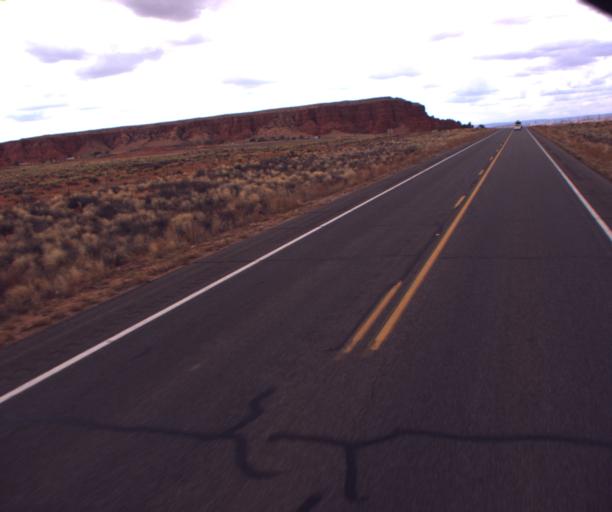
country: US
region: Arizona
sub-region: Navajo County
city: Kayenta
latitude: 36.7791
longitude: -109.9990
